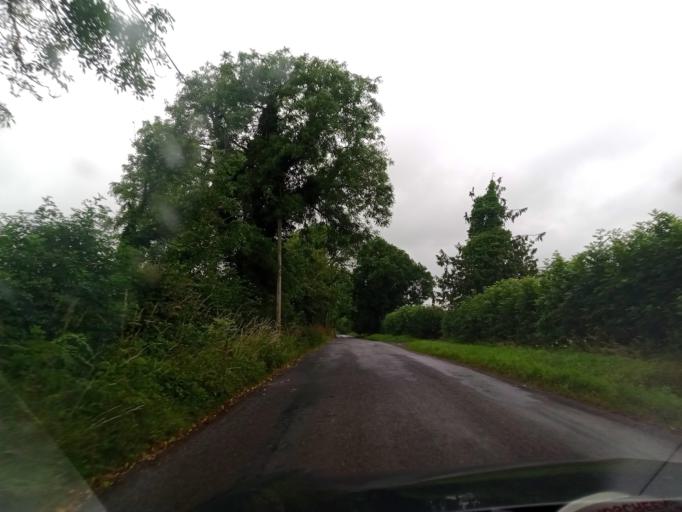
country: IE
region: Leinster
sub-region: Laois
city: Abbeyleix
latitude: 52.9177
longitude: -7.2879
